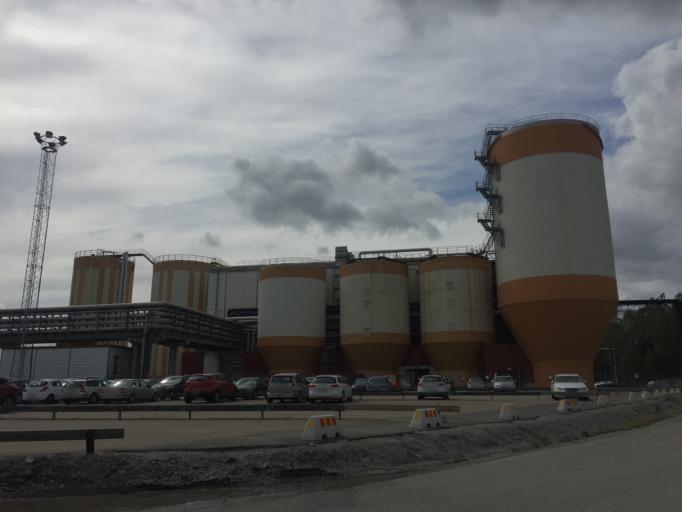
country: SE
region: OErebro
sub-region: Lindesbergs Kommun
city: Frovi
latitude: 59.4823
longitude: 15.3240
